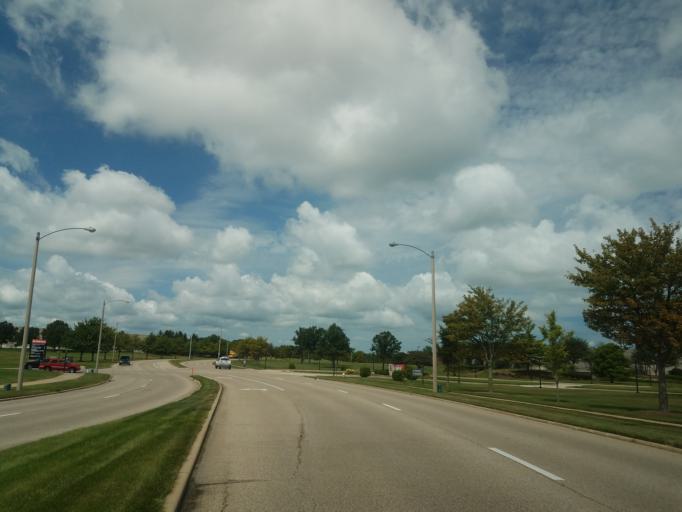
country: US
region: Illinois
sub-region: McLean County
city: Bloomington
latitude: 40.4612
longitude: -88.9514
